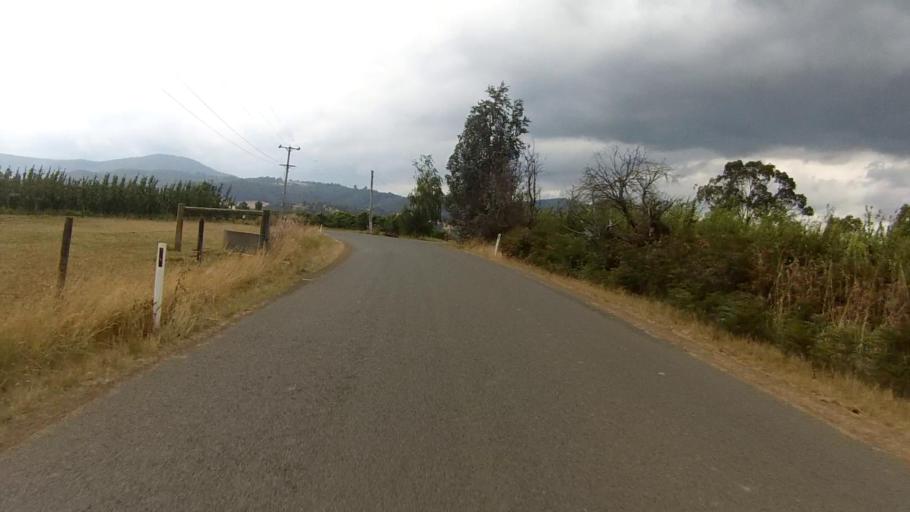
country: AU
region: Tasmania
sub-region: Huon Valley
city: Huonville
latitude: -42.9923
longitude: 147.0627
